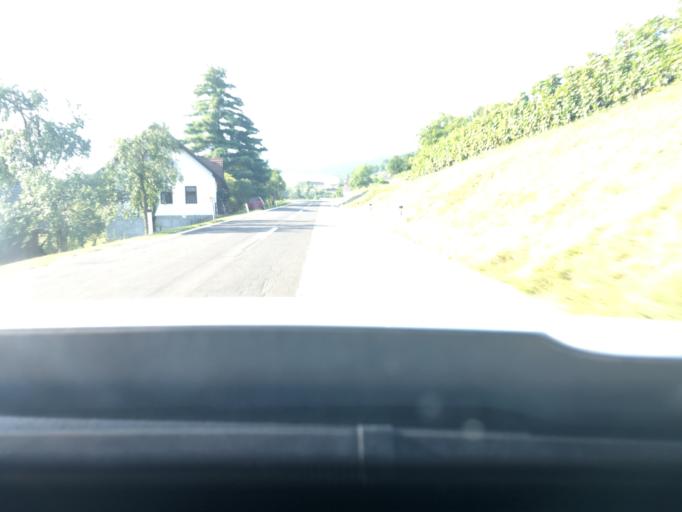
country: SI
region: Metlika
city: Metlika
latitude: 45.6750
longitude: 15.2851
